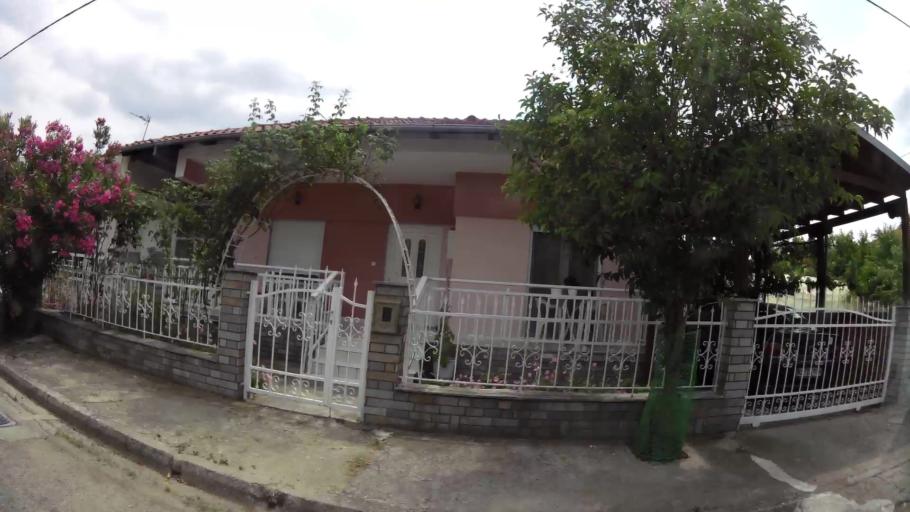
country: GR
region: Central Macedonia
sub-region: Nomos Pierias
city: Kallithea
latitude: 40.2710
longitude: 22.5794
